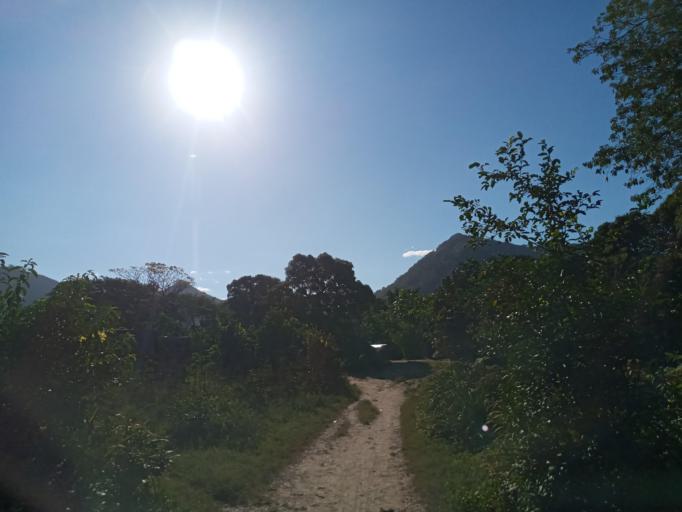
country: MG
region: Anosy
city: Fort Dauphin
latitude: -24.8258
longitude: 47.0447
